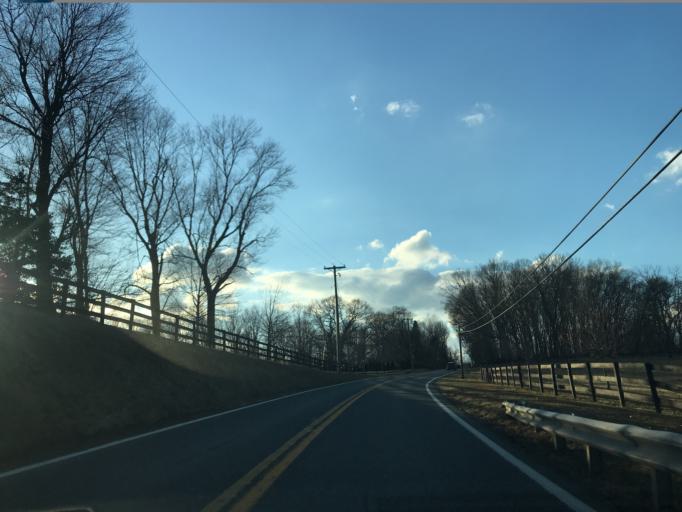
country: US
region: Pennsylvania
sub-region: York County
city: Susquehanna Trails
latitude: 39.7152
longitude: -76.3765
